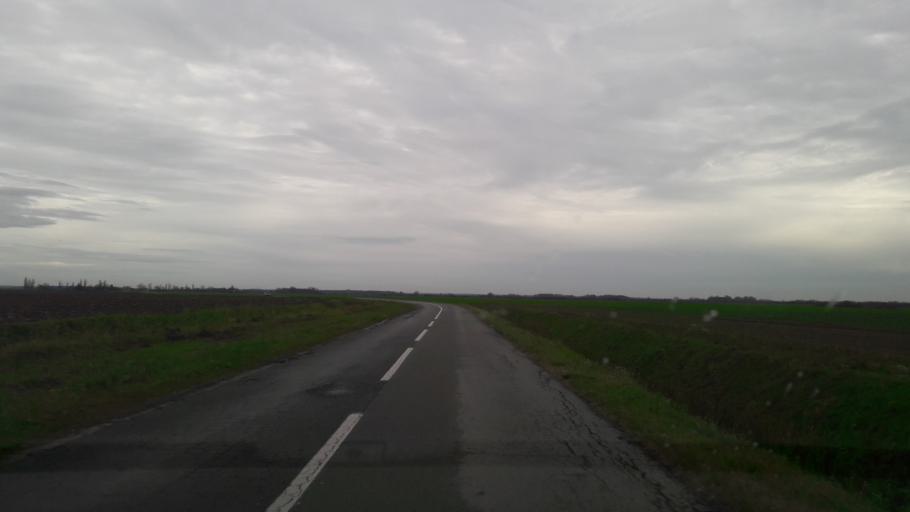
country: HR
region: Virovitick-Podravska
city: Zdenci
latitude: 45.5977
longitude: 17.9772
